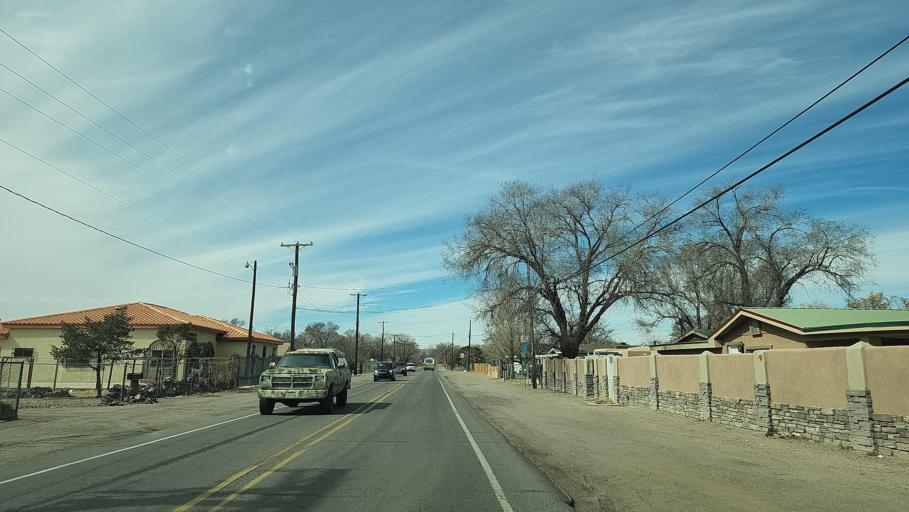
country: US
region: New Mexico
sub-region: Bernalillo County
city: South Valley
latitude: 35.0363
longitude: -106.6874
